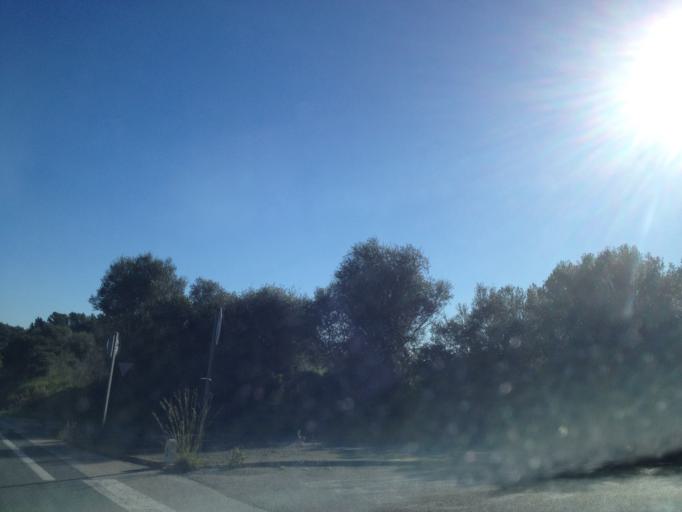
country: ES
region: Balearic Islands
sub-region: Illes Balears
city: Sineu
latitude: 39.6548
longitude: 3.0344
